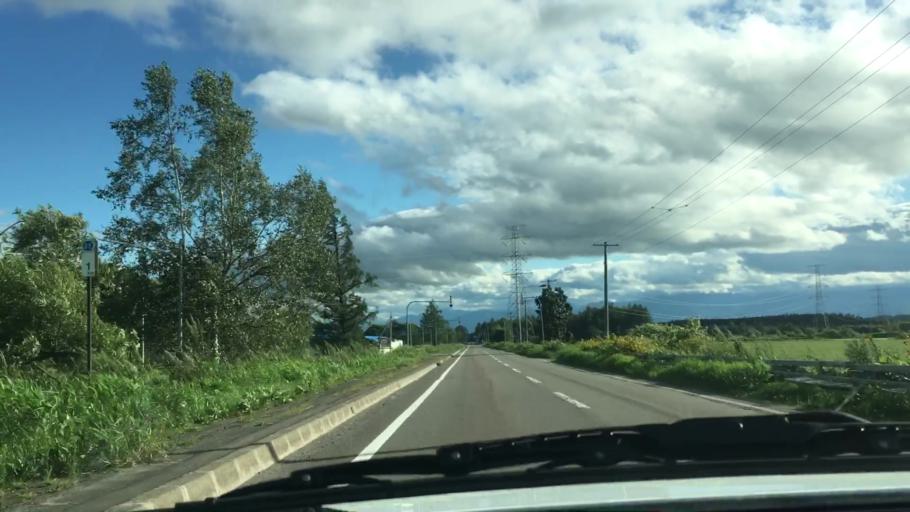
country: JP
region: Hokkaido
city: Otofuke
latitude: 43.1780
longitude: 143.0077
